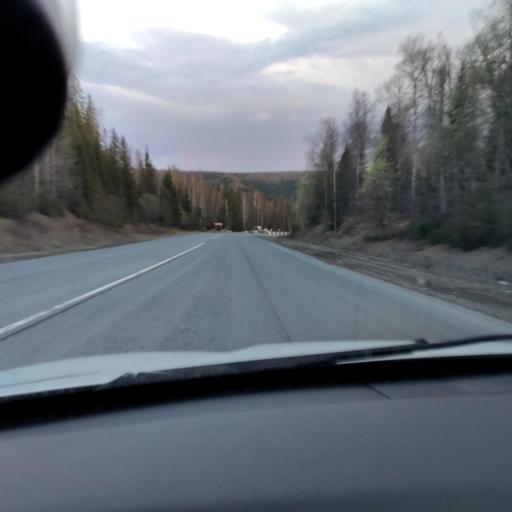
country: RU
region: Perm
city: Gremyachinsk
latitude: 58.4482
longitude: 57.8724
